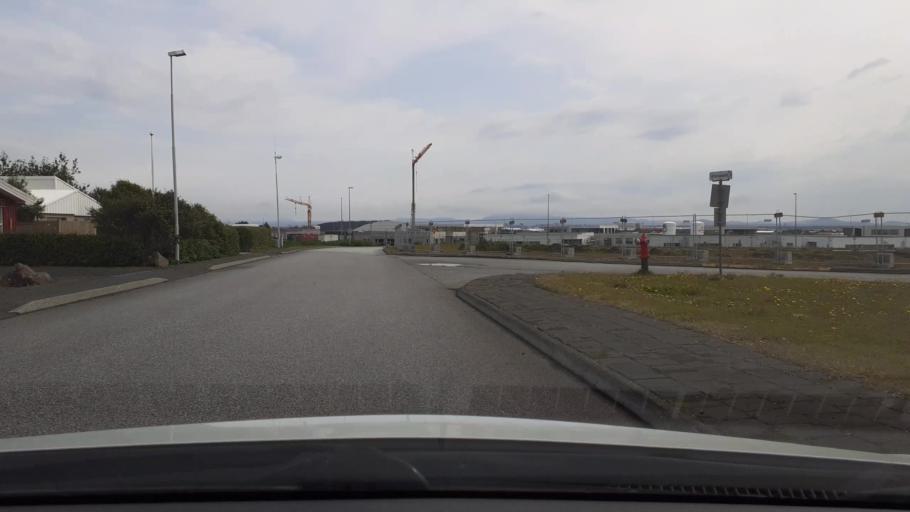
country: IS
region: Southern Peninsula
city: Reykjanesbaer
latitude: 63.9962
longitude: -22.5704
